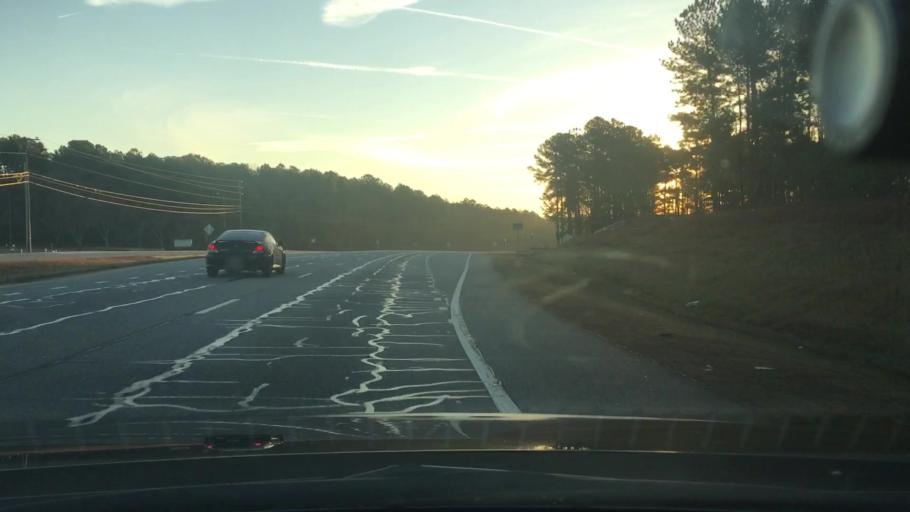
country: US
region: Georgia
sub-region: Fayette County
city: Peachtree City
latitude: 33.4073
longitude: -84.6703
